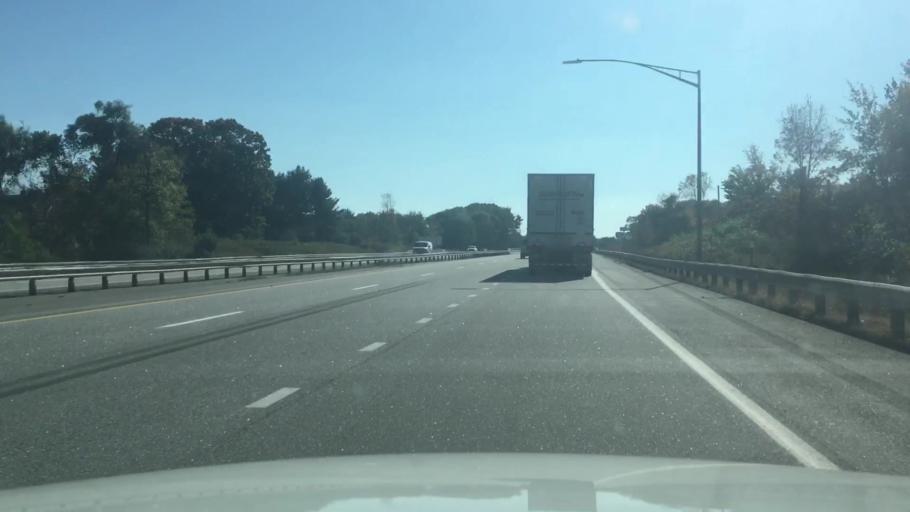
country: US
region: Maine
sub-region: Cumberland County
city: Falmouth
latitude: 43.7175
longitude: -70.3060
